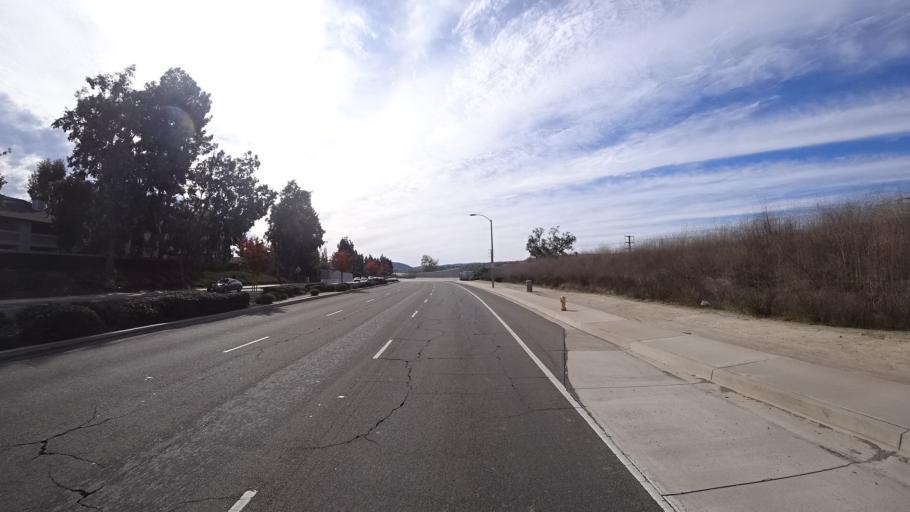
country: US
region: California
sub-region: Orange County
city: Aliso Viejo
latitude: 33.5770
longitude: -117.7111
